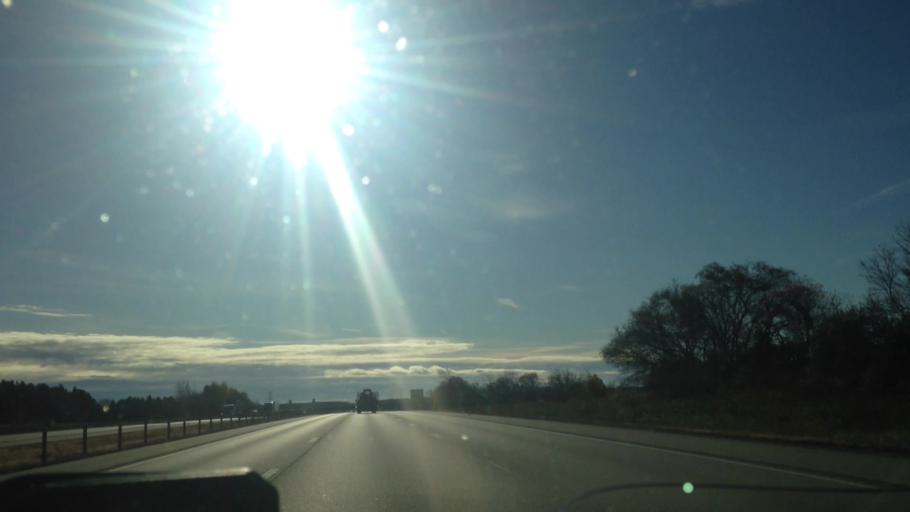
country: US
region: Wisconsin
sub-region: Washington County
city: Richfield
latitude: 43.2251
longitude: -88.1620
